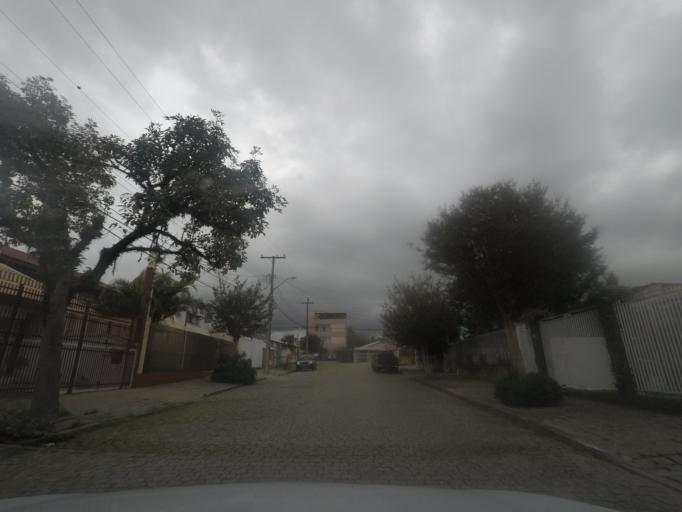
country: BR
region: Parana
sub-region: Curitiba
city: Curitiba
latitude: -25.4394
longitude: -49.2434
